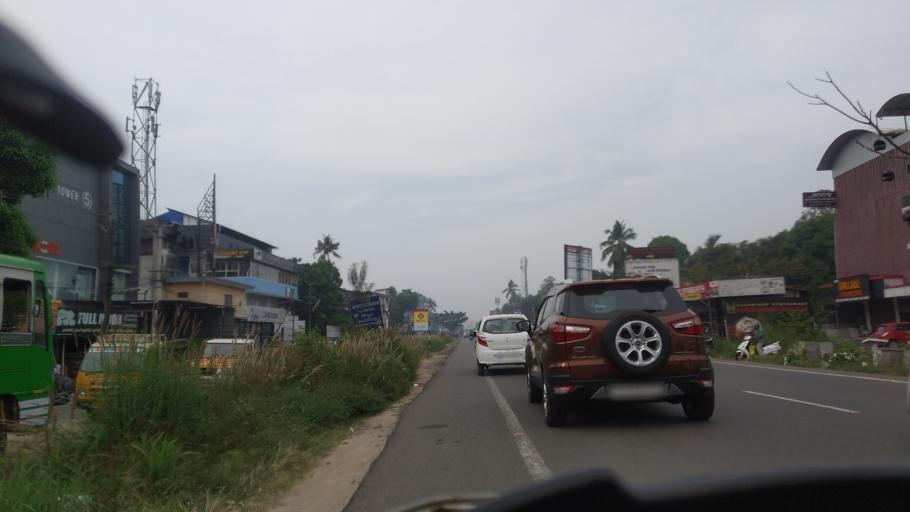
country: IN
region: Kerala
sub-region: Ernakulam
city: Elur
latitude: 10.0513
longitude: 76.2937
